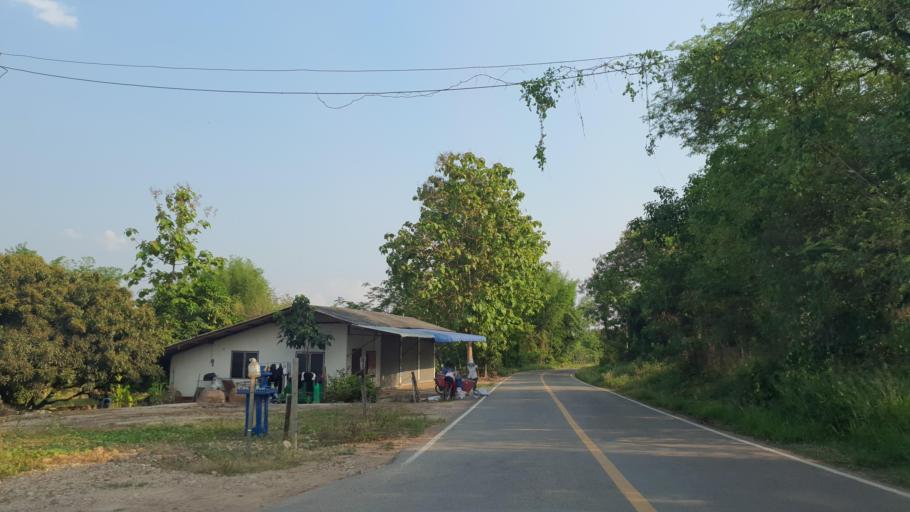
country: TH
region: Chiang Mai
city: Mae Wang
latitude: 18.6475
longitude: 98.8142
